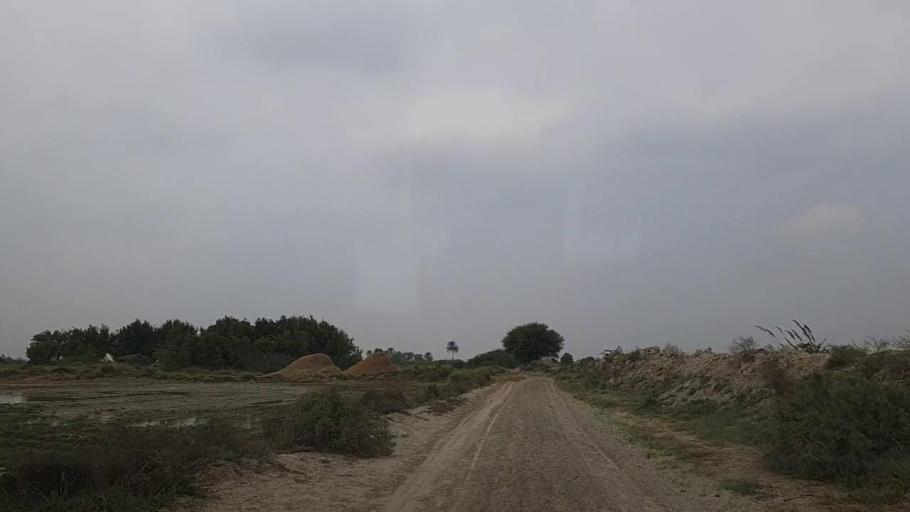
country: PK
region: Sindh
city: Mirpur Sakro
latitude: 24.5933
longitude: 67.6992
